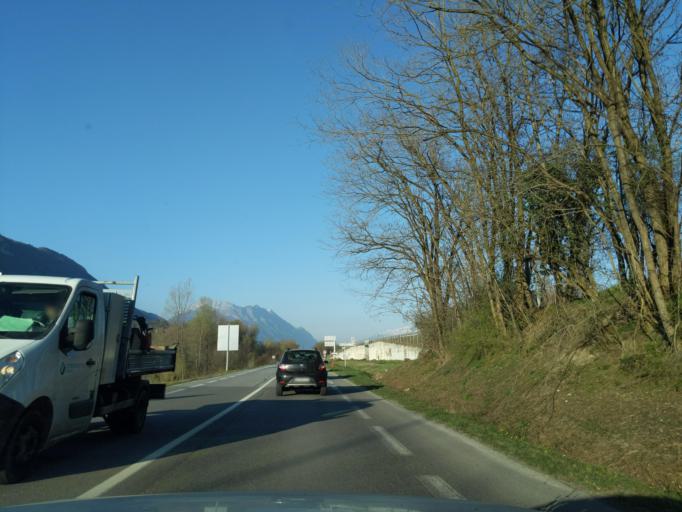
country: FR
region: Rhone-Alpes
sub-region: Departement de la Savoie
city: Montmelian
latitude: 45.4901
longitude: 6.0434
